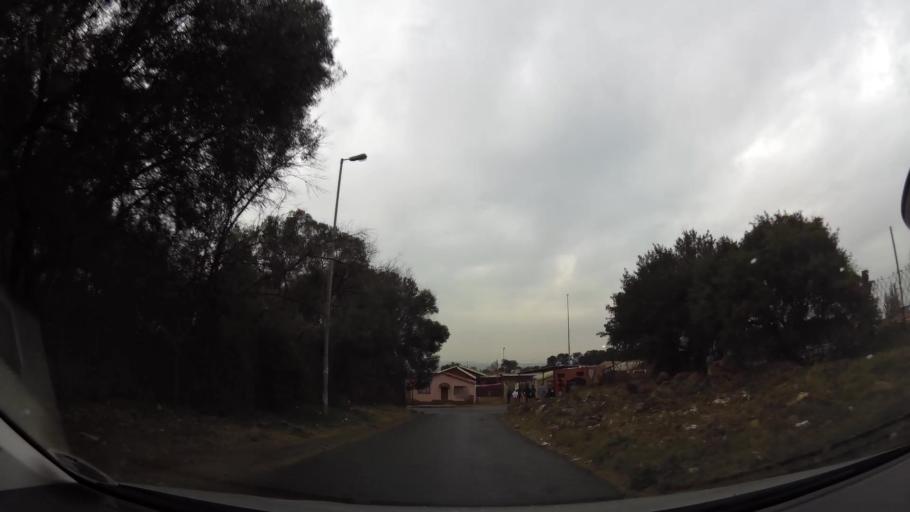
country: ZA
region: Gauteng
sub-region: City of Johannesburg Metropolitan Municipality
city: Soweto
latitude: -26.2443
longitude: 27.8699
